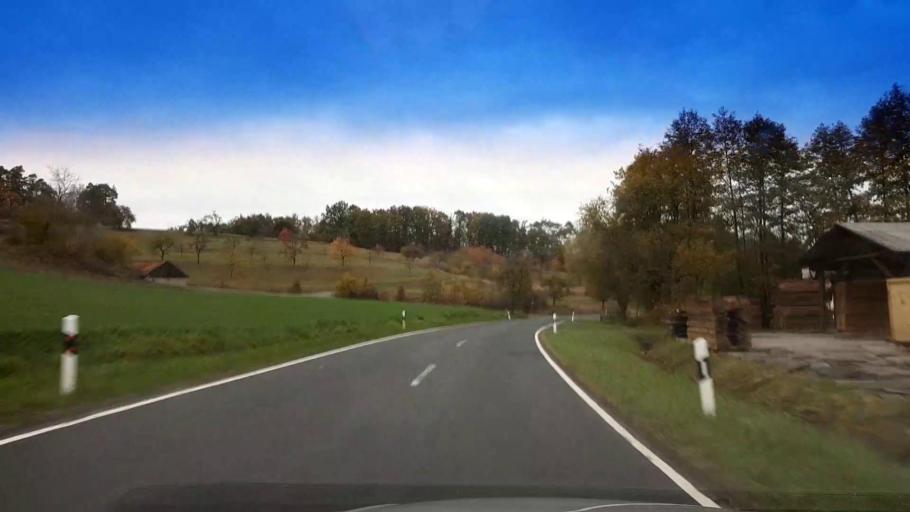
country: DE
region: Bavaria
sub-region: Regierungsbezirk Unterfranken
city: Stettfeld
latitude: 49.9501
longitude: 10.7049
